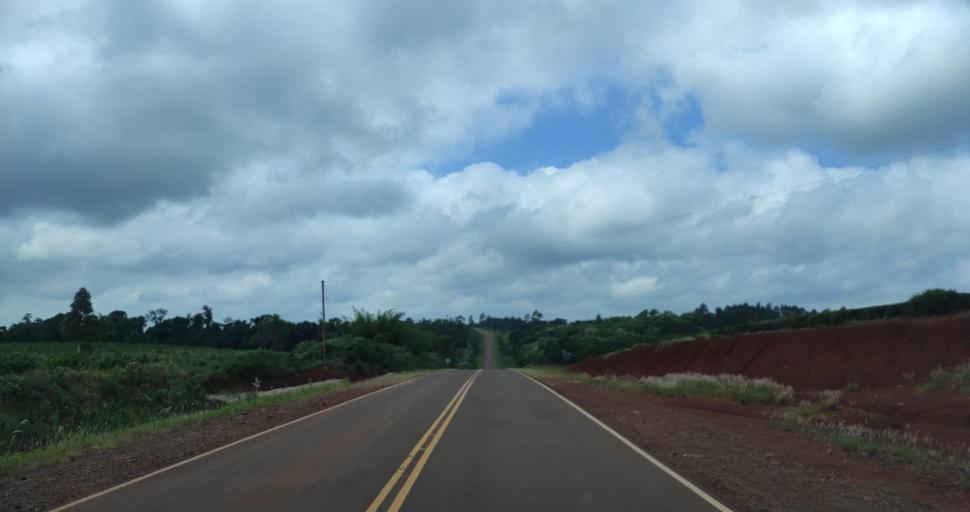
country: AR
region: Misiones
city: Campo Grande
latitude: -27.3110
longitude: -54.8996
